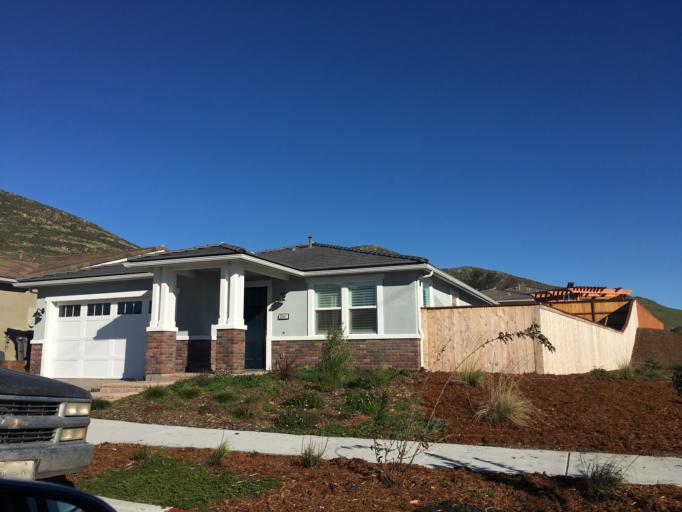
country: US
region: California
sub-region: San Luis Obispo County
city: San Luis Obispo
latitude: 35.2558
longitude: -120.6591
